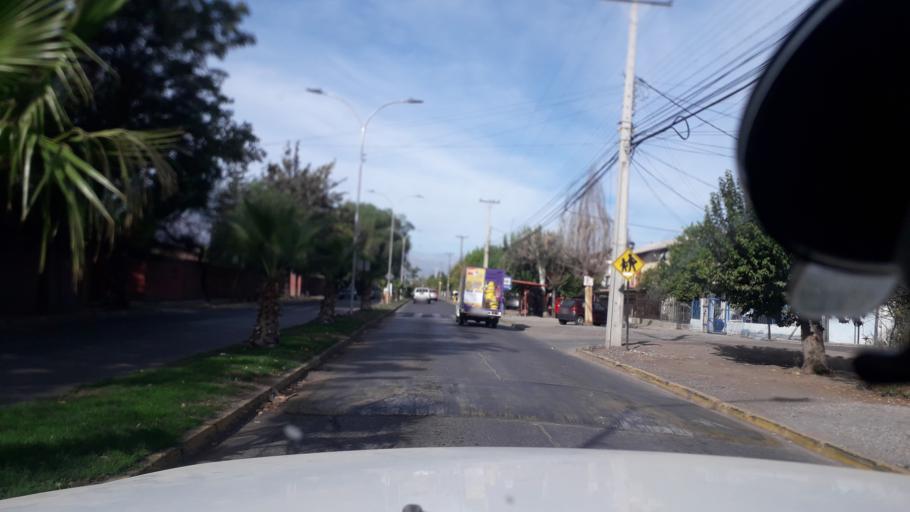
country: CL
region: Valparaiso
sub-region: Provincia de San Felipe
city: San Felipe
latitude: -32.7490
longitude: -70.7143
